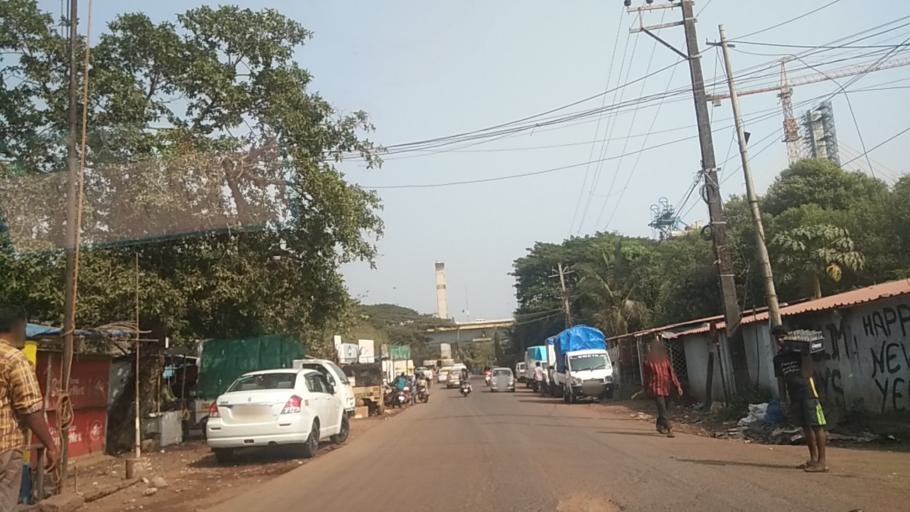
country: IN
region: Goa
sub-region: North Goa
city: Panaji
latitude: 15.5055
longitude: 73.8347
